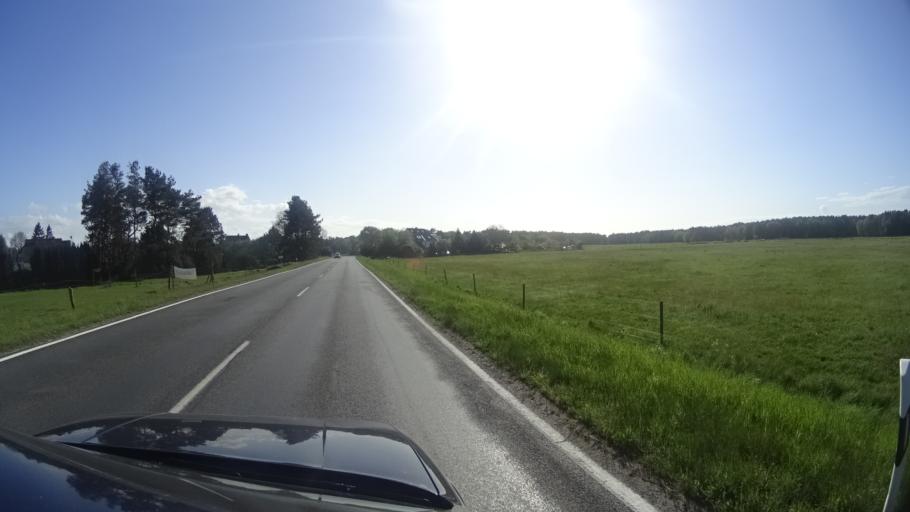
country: DE
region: Mecklenburg-Vorpommern
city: Ostseebad Prerow
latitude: 54.4123
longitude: 12.5773
